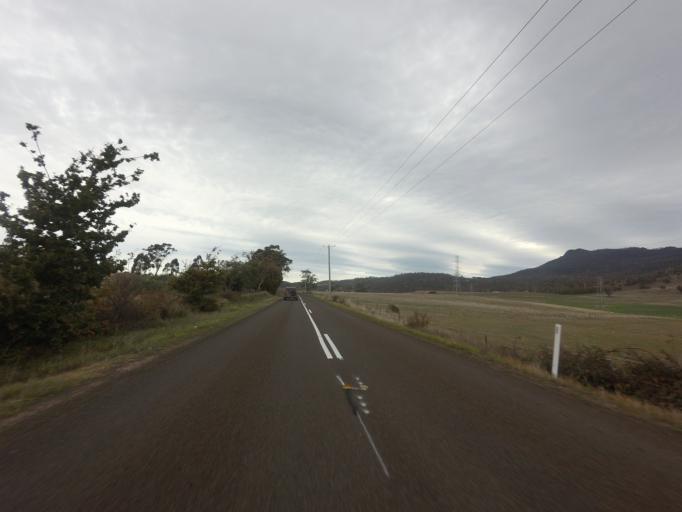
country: AU
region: Tasmania
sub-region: Brighton
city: Bridgewater
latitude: -42.6652
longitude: 147.1320
